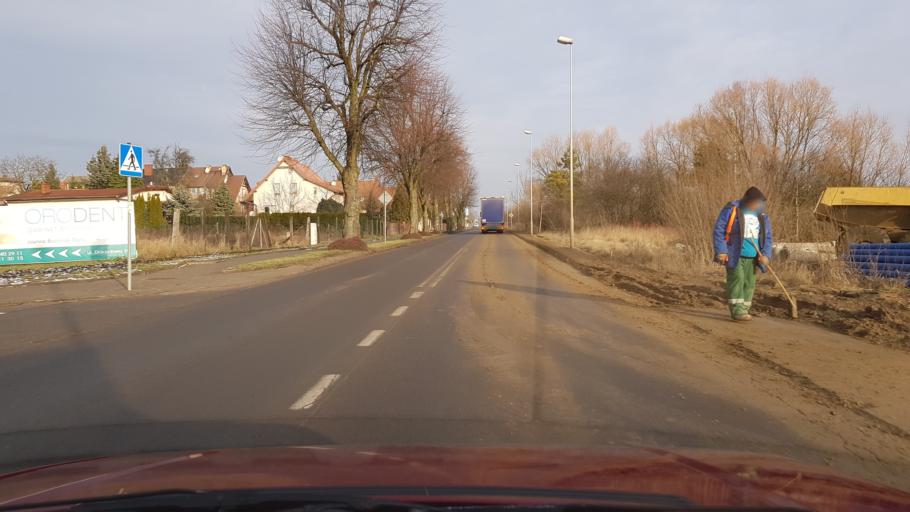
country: PL
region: West Pomeranian Voivodeship
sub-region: Powiat policki
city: Police
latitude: 53.4909
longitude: 14.5846
